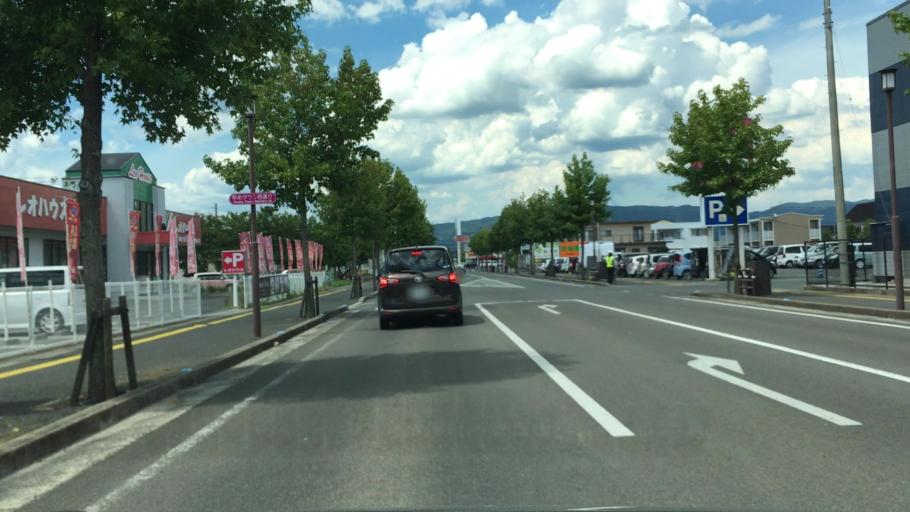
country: JP
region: Saga Prefecture
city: Saga-shi
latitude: 33.2745
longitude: 130.3054
